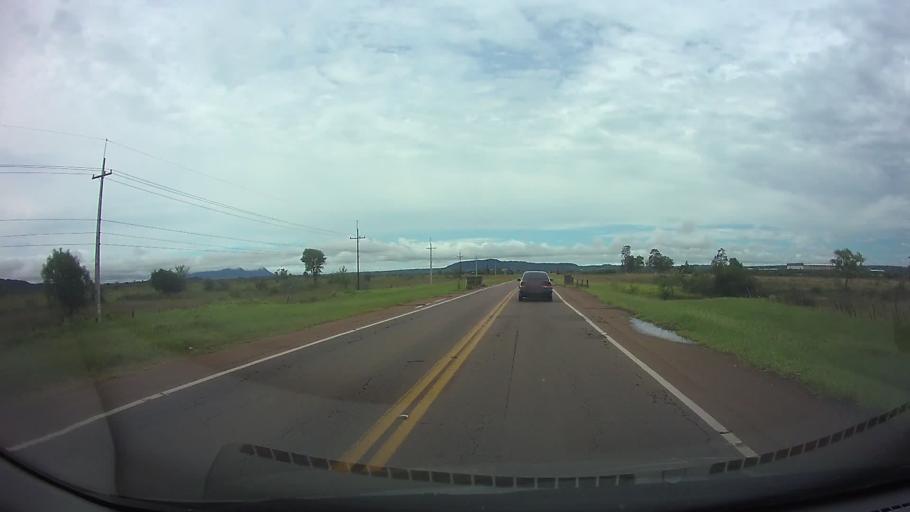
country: PY
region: Paraguari
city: Carapegua
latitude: -25.7286
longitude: -57.2060
